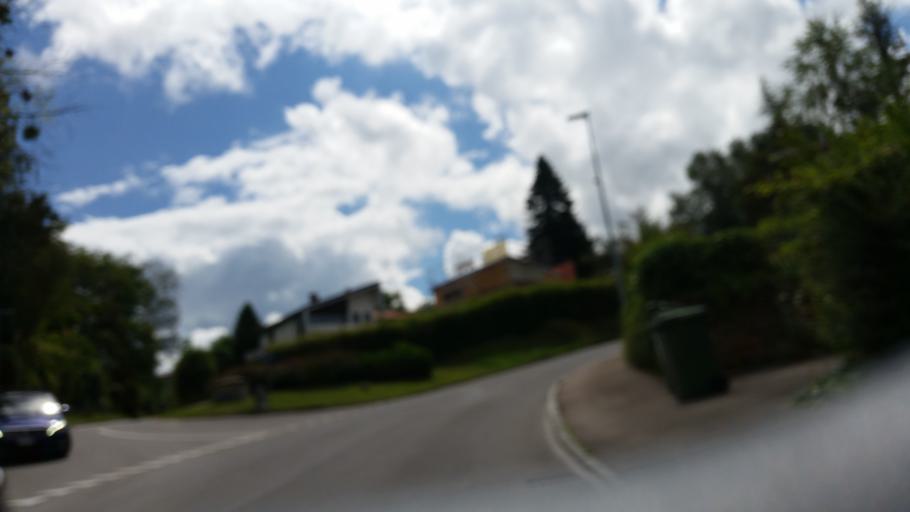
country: CH
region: Vaud
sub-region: Jura-Nord vaudois District
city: Yverdon-les-Bains
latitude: 46.7779
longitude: 6.6643
